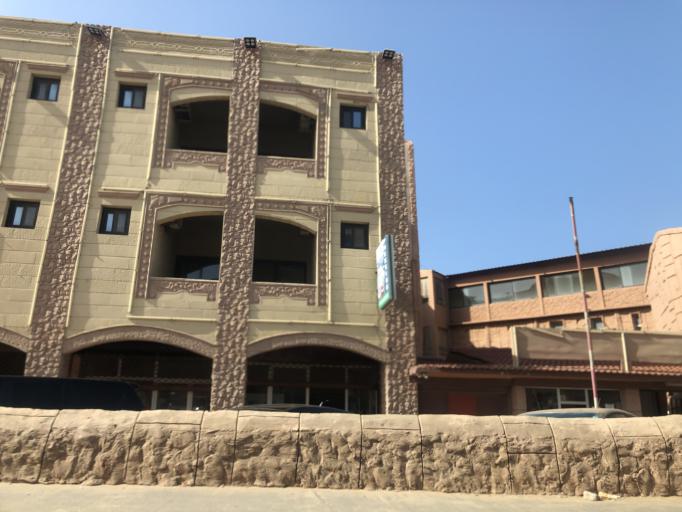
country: SN
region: Dakar
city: Mermoz Boabab
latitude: 14.7542
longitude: -17.4954
